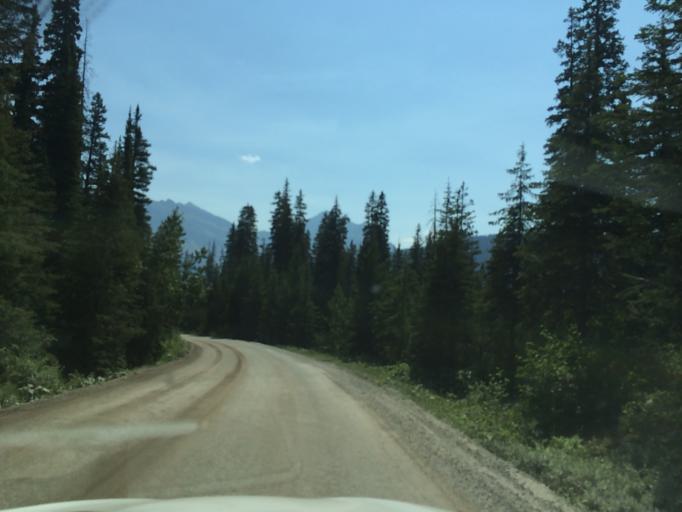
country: US
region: Montana
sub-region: Flathead County
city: Columbia Falls
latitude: 48.6909
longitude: -113.6689
